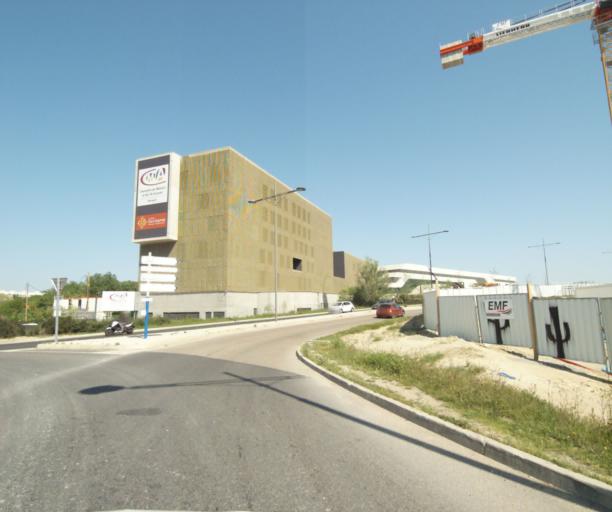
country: FR
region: Languedoc-Roussillon
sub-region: Departement de l'Herault
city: Juvignac
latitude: 43.6221
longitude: 3.8230
